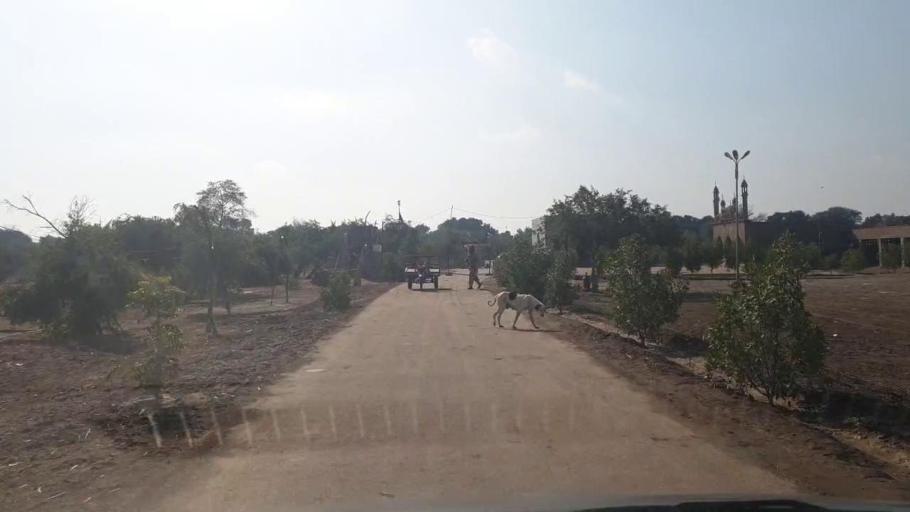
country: PK
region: Sindh
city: Shahdadpur
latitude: 25.8820
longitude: 68.5633
